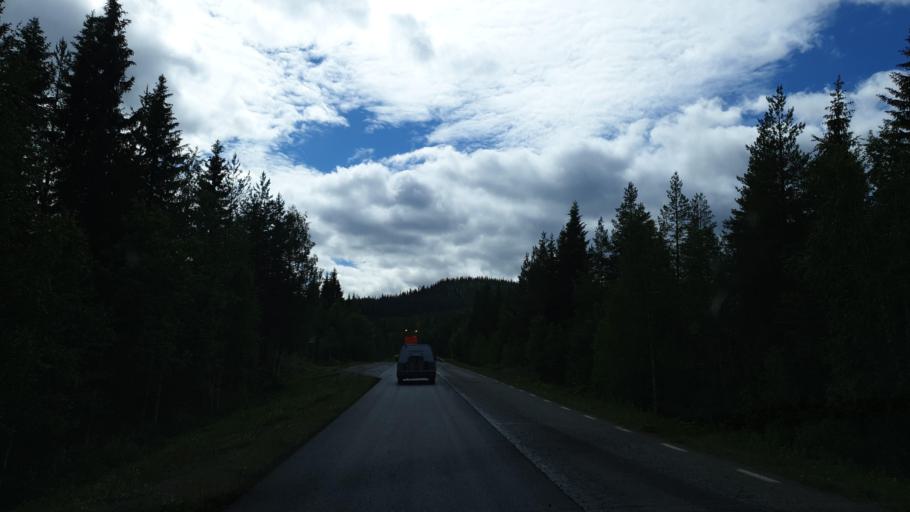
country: SE
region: Vaesterbotten
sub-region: Vilhelmina Kommun
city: Sjoberg
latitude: 64.8996
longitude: 15.8604
